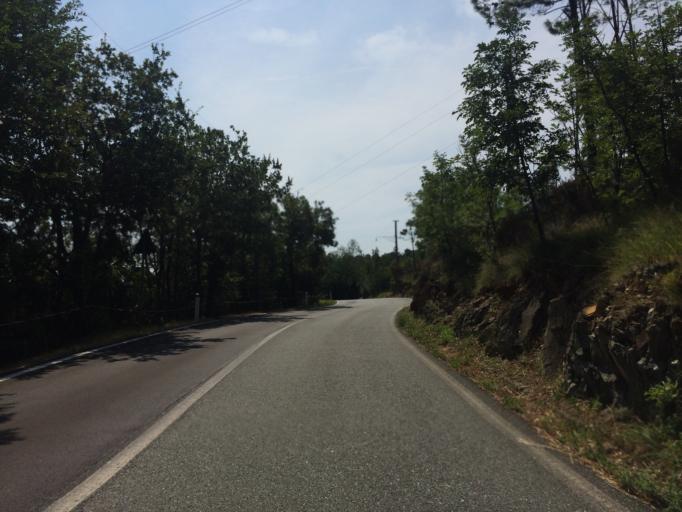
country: IT
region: Liguria
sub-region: Provincia di Genova
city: Sciarborasca
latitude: 44.3961
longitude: 8.6183
